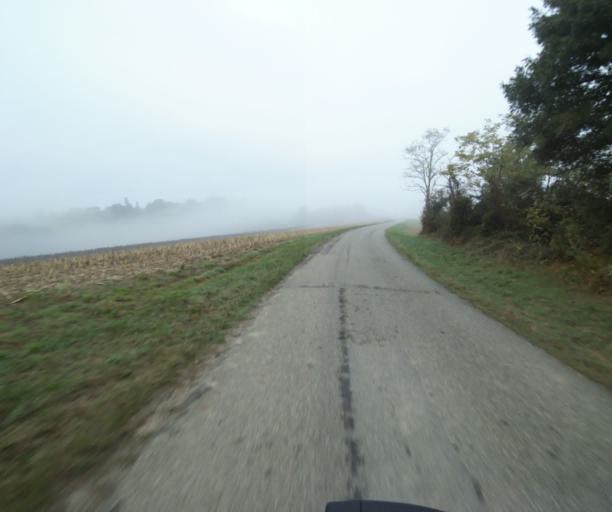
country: FR
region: Midi-Pyrenees
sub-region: Departement du Tarn-et-Garonne
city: Saint-Nauphary
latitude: 43.9449
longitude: 1.4081
